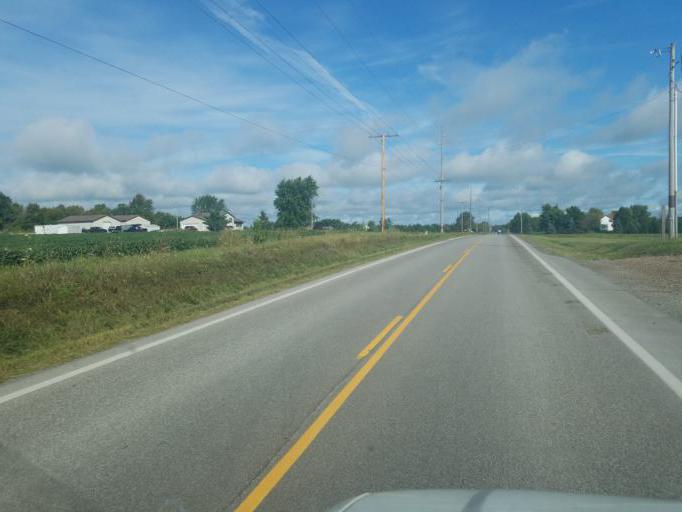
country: US
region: Ohio
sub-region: Wayne County
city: West Salem
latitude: 41.0122
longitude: -82.1186
